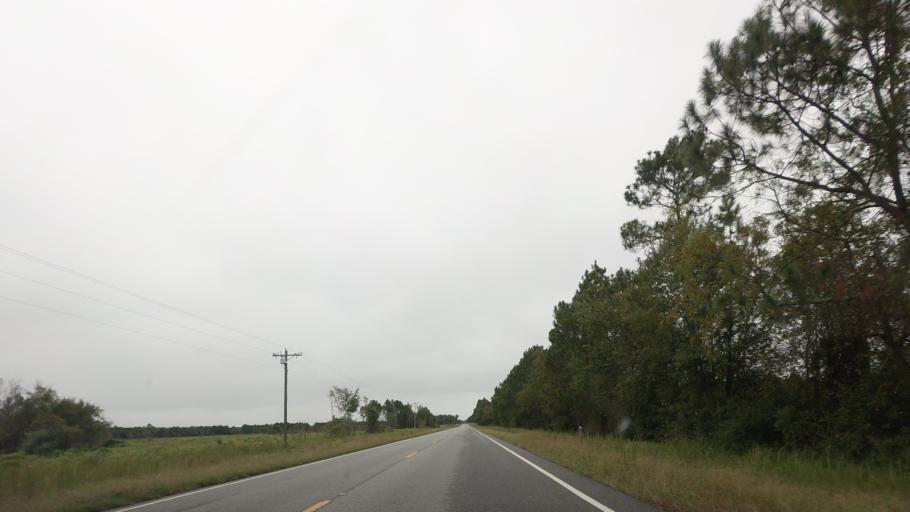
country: US
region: Georgia
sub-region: Berrien County
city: Nashville
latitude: 31.3152
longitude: -83.2317
